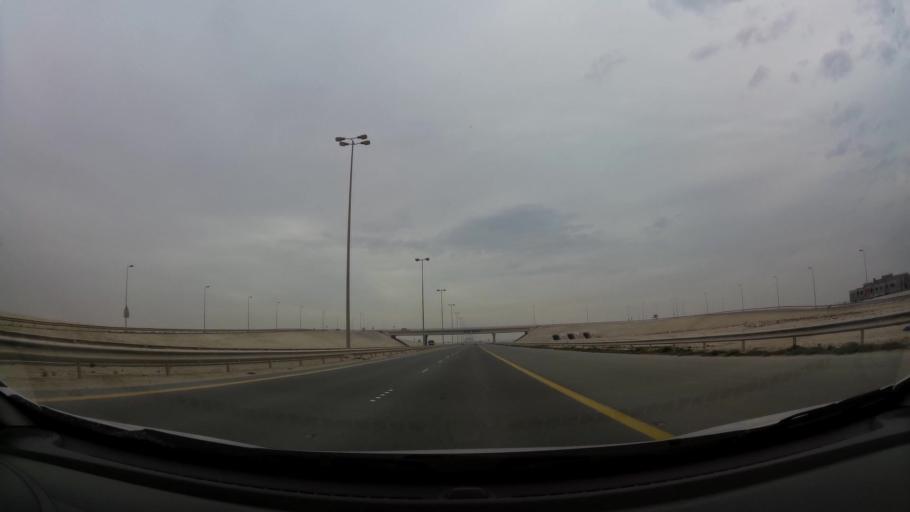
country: BH
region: Central Governorate
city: Dar Kulayb
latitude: 25.9912
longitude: 50.6026
